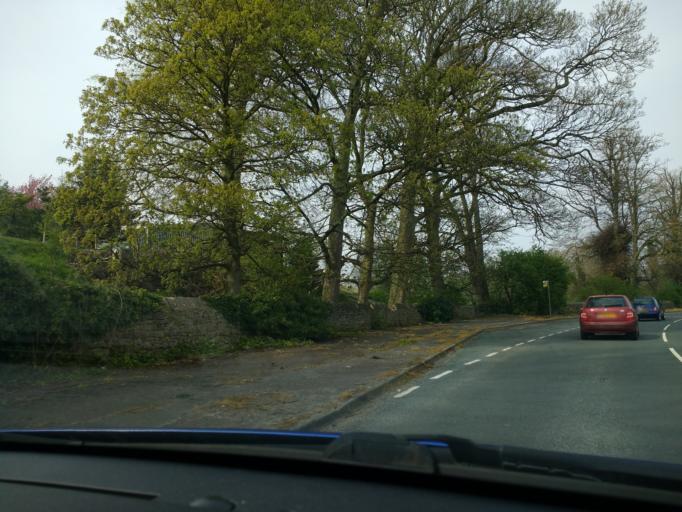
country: GB
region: England
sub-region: Lancashire
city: Lancaster
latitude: 54.0230
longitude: -2.8097
